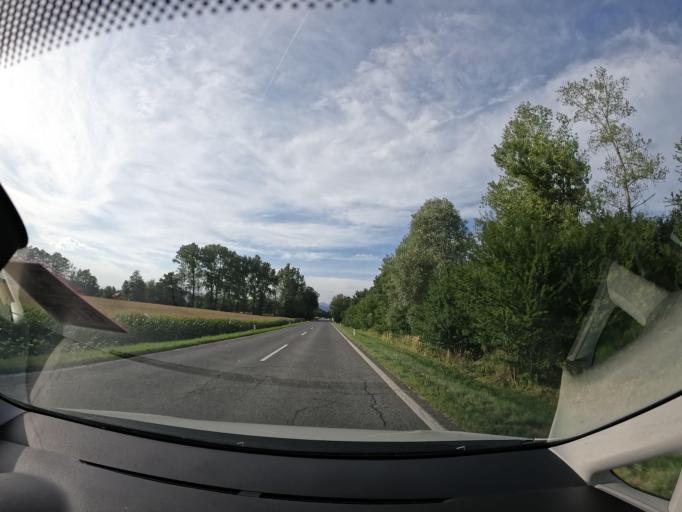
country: AT
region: Carinthia
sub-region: Politischer Bezirk Volkermarkt
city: Eberndorf
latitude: 46.5971
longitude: 14.6345
